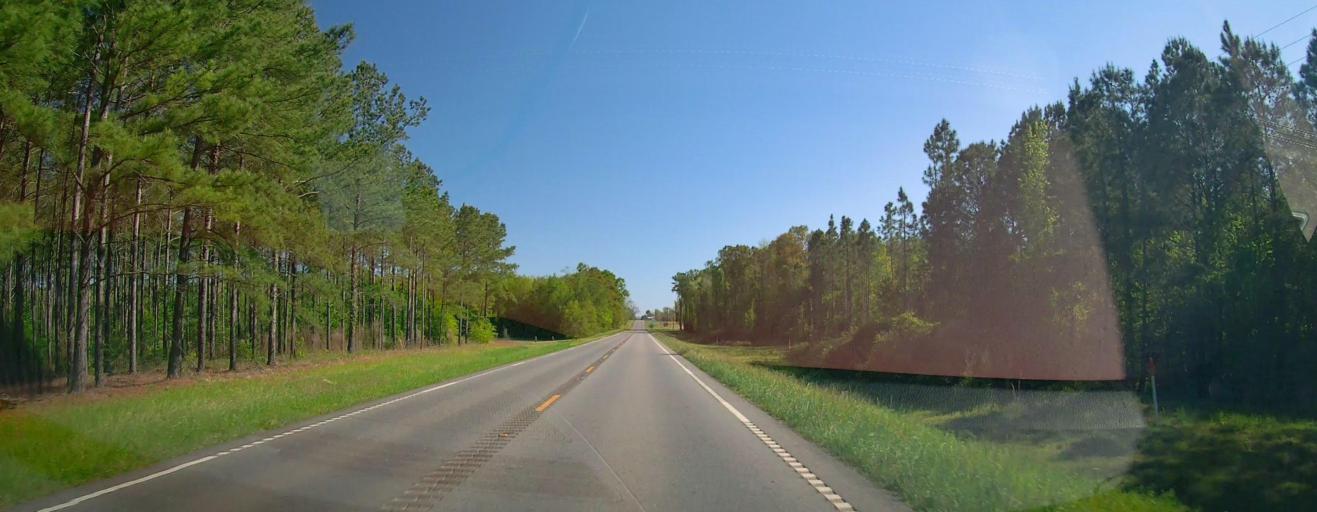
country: US
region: Georgia
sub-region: Pulaski County
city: Hawkinsville
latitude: 32.1218
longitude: -83.5008
